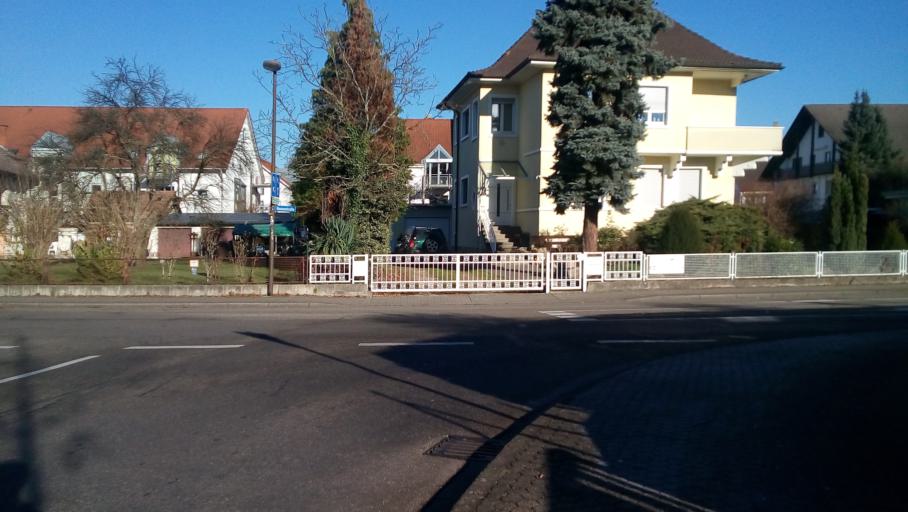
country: DE
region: Baden-Wuerttemberg
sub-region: Freiburg Region
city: Achern
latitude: 48.6304
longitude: 8.0773
